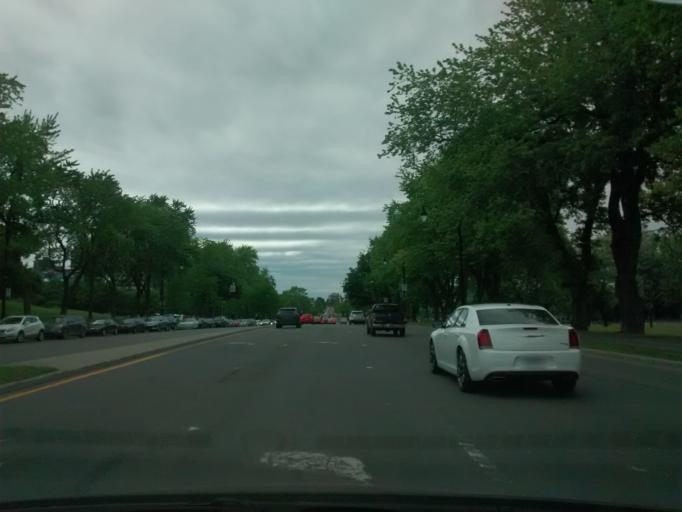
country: CA
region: Quebec
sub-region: Montreal
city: Montreal
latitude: 45.5150
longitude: -73.5854
